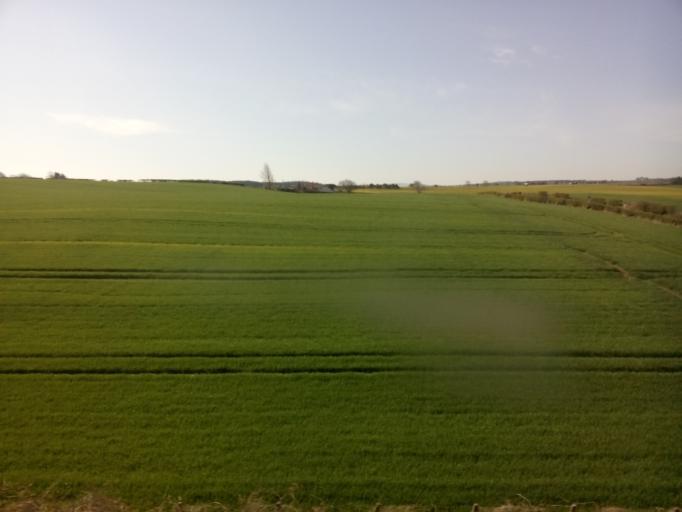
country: GB
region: Scotland
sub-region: East Lothian
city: North Berwick
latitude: 56.0082
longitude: -2.7356
